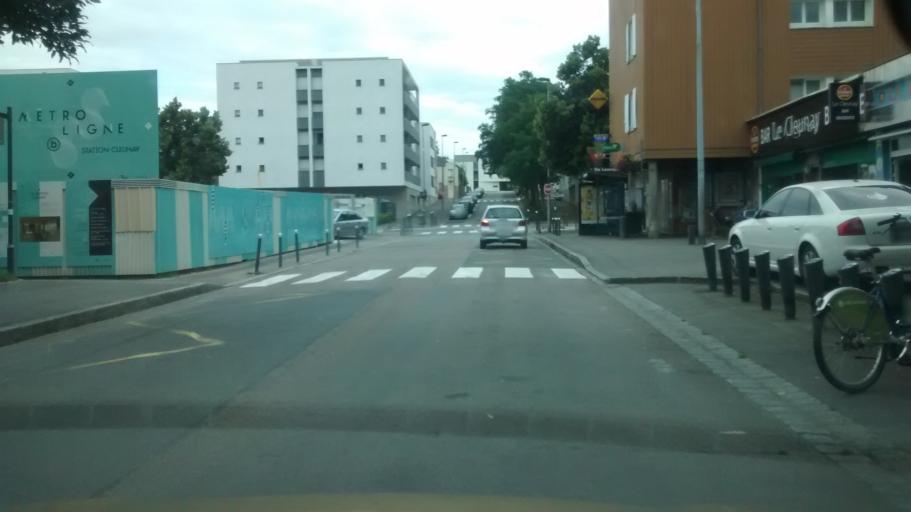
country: FR
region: Brittany
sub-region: Departement d'Ille-et-Vilaine
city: Rennes
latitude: 48.1010
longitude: -1.7070
